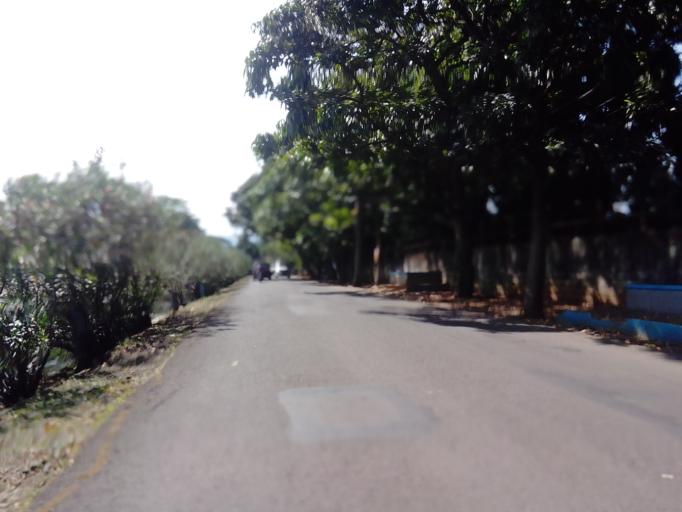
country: ID
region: West Java
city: Bandung
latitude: -6.9405
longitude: 107.6697
